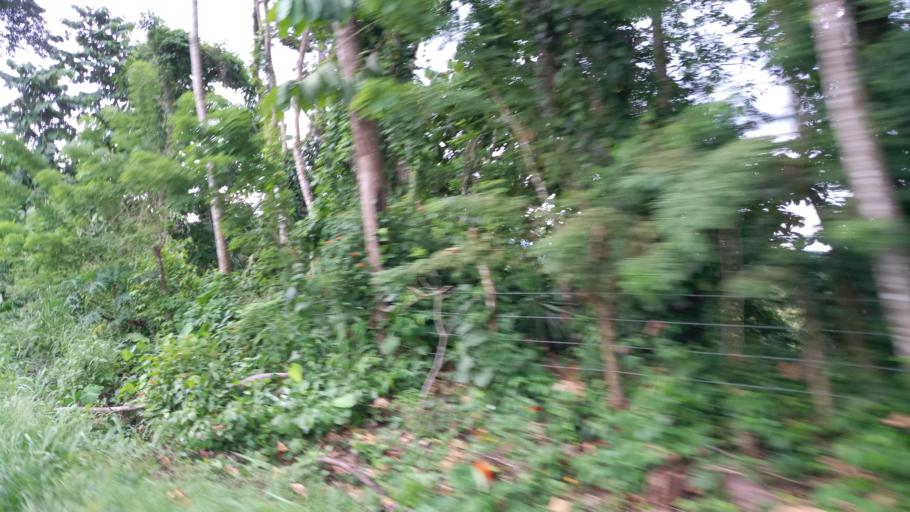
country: CR
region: Alajuela
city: Pocosol
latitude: 10.3725
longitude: -84.5697
